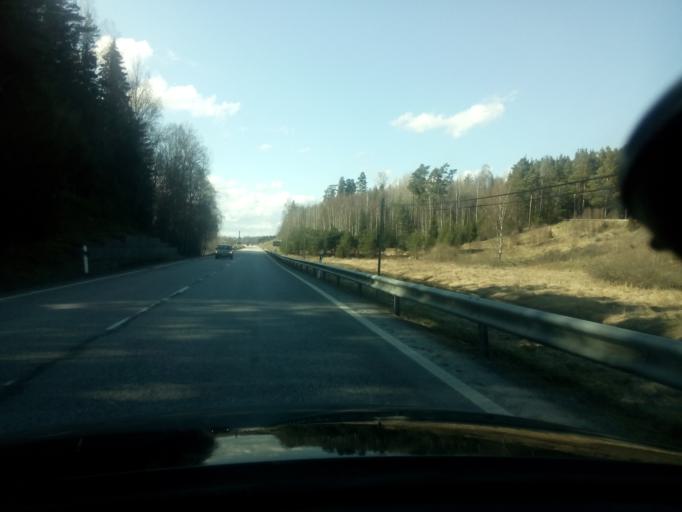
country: SE
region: Soedermanland
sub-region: Flens Kommun
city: Malmkoping
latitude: 59.1169
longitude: 16.7594
